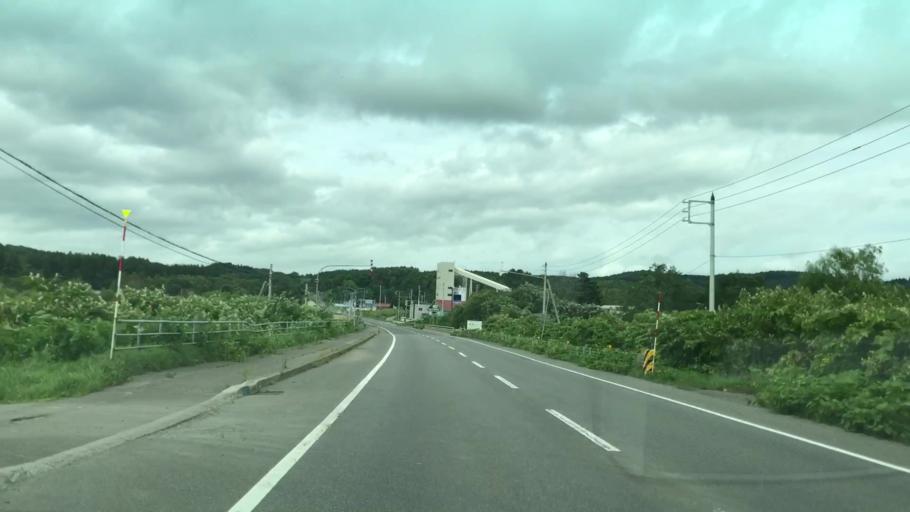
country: JP
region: Hokkaido
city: Niseko Town
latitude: 42.9189
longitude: 140.7447
